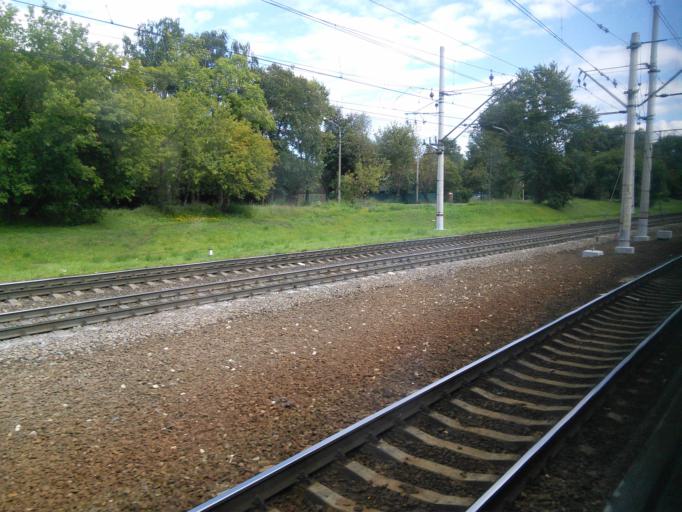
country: RU
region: Moscow
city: Zhulebino
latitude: 55.7044
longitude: 37.8517
